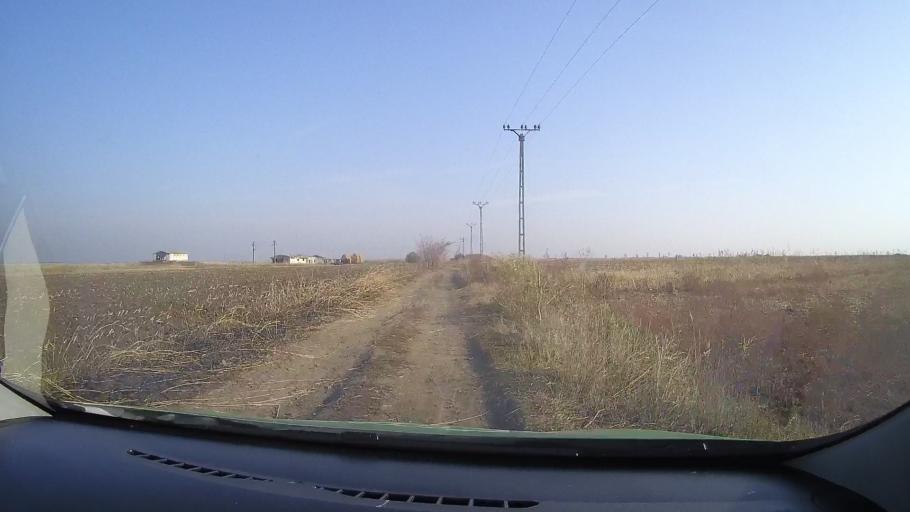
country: RO
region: Arad
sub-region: Comuna Pilu
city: Pilu
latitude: 46.5432
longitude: 21.3290
